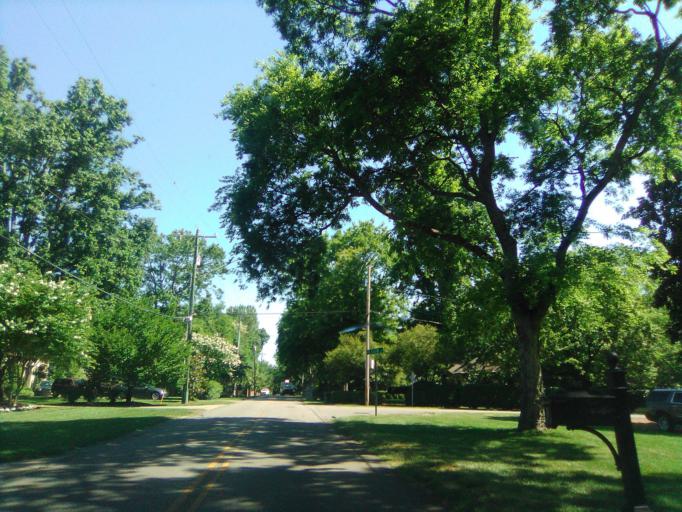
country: US
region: Tennessee
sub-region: Davidson County
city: Belle Meade
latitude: 36.1219
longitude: -86.8302
